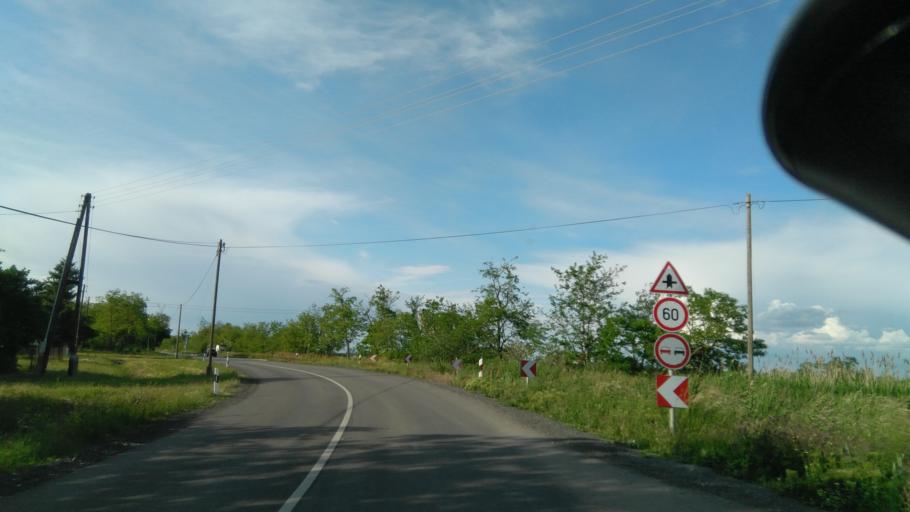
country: HU
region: Bekes
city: Elek
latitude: 46.5817
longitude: 21.2757
